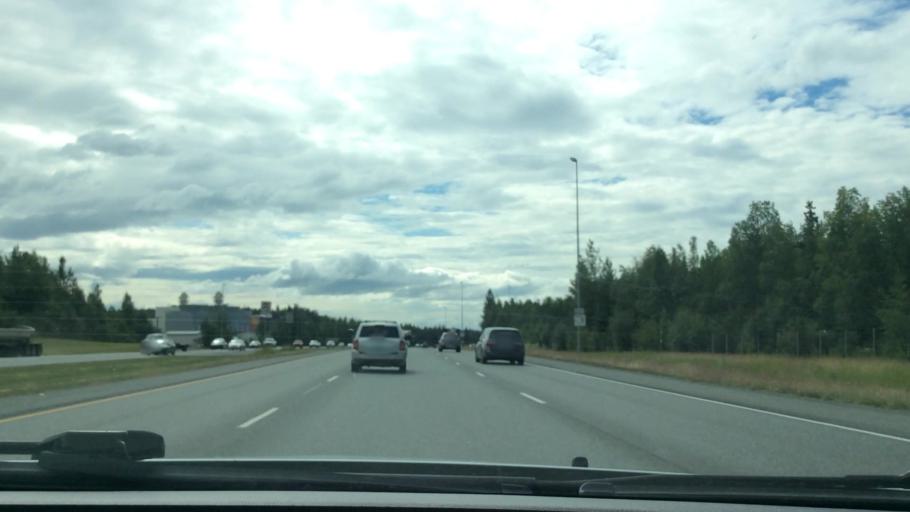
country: US
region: Alaska
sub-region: Anchorage Municipality
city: Elmendorf Air Force Base
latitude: 61.2339
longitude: -149.7069
